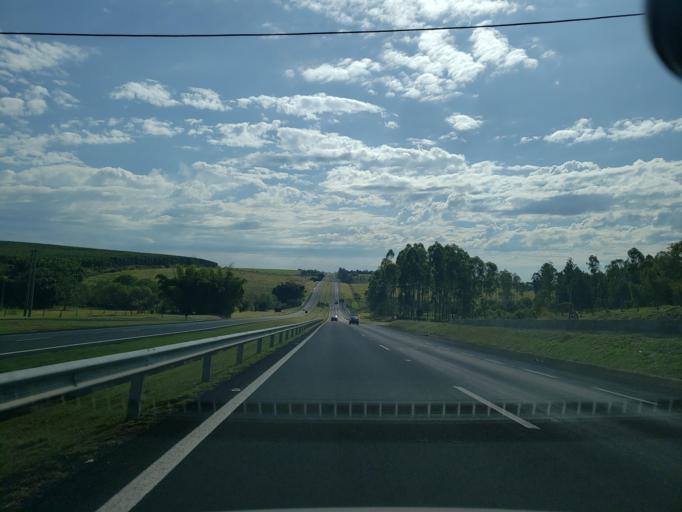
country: BR
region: Sao Paulo
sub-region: Pirajui
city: Pirajui
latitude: -21.9760
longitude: -49.4521
